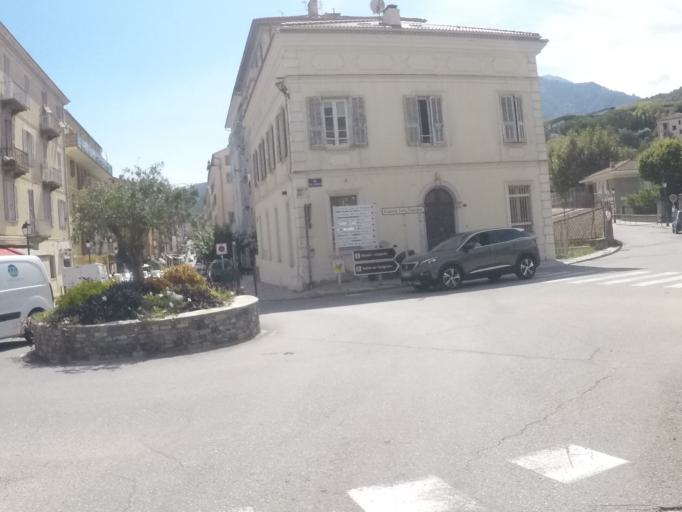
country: FR
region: Corsica
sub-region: Departement de la Haute-Corse
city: Corte
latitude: 42.3091
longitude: 9.1498
